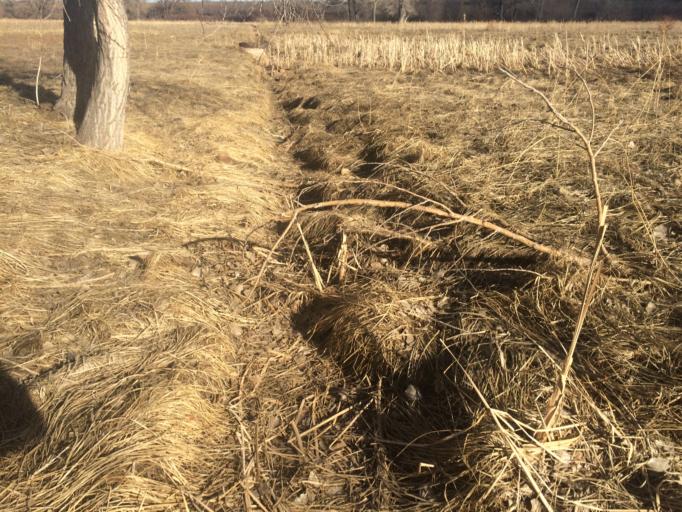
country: US
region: Colorado
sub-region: Boulder County
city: Superior
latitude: 39.9715
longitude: -105.2270
